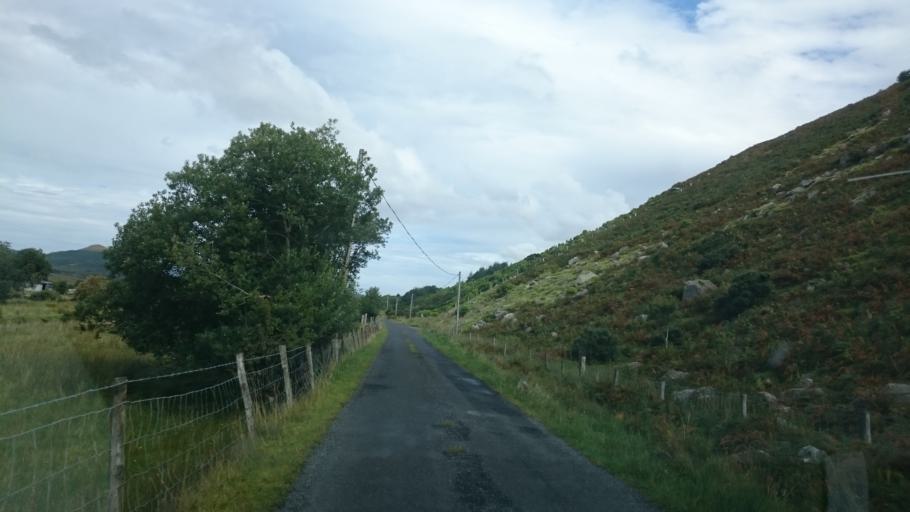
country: IE
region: Connaught
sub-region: Maigh Eo
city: Westport
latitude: 53.9661
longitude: -9.5705
